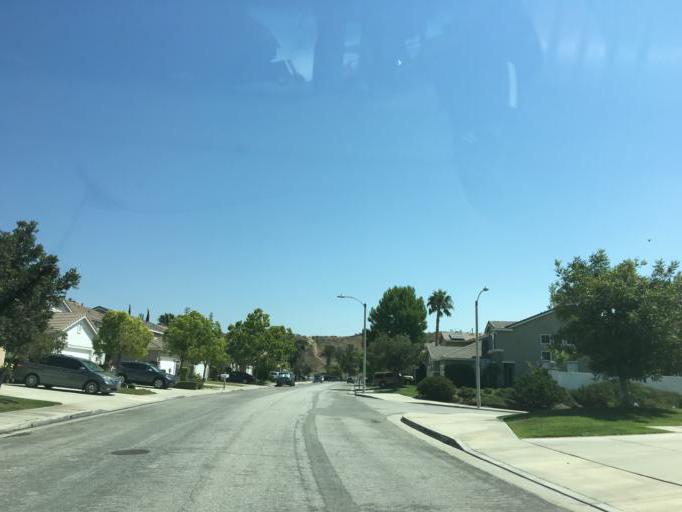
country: US
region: California
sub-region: Los Angeles County
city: Santa Clarita
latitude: 34.3947
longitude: -118.5880
